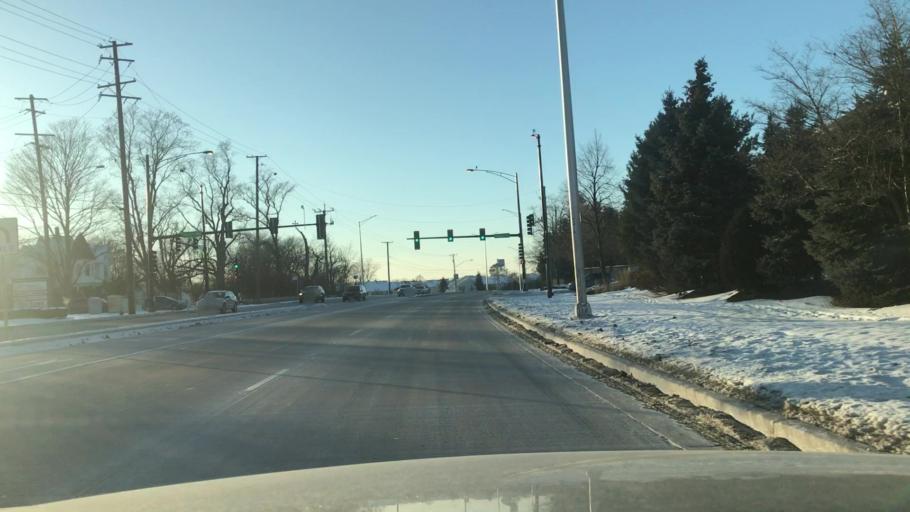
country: US
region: Illinois
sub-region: Kane County
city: Aurora
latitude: 41.7588
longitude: -88.2508
